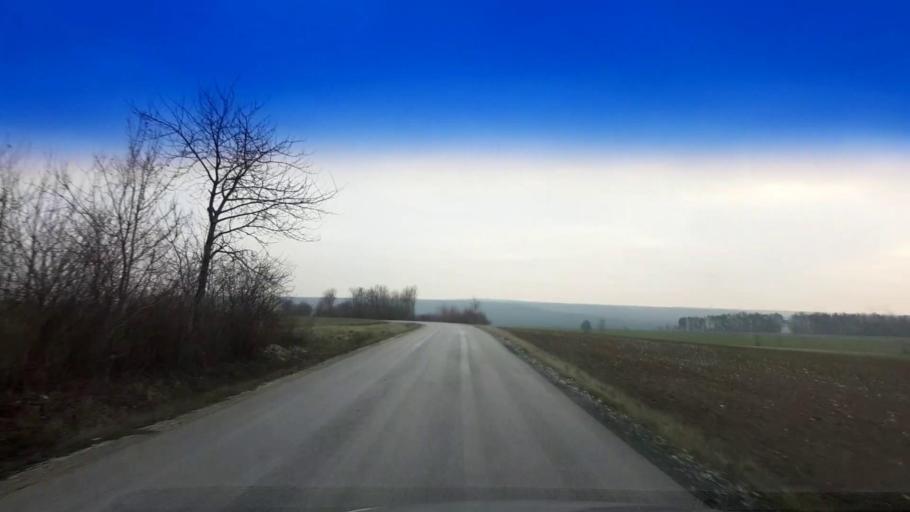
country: DE
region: Bavaria
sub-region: Upper Franconia
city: Hallerndorf
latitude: 49.7762
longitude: 10.9855
